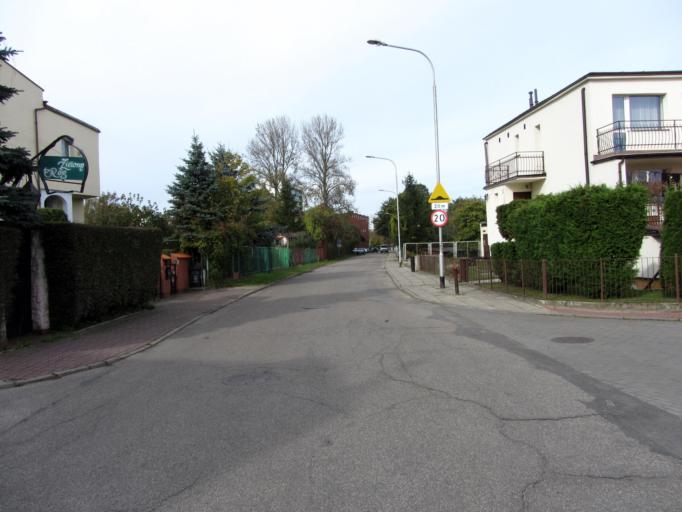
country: PL
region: West Pomeranian Voivodeship
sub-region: Powiat kolobrzeski
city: Kolobrzeg
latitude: 54.1708
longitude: 15.5760
